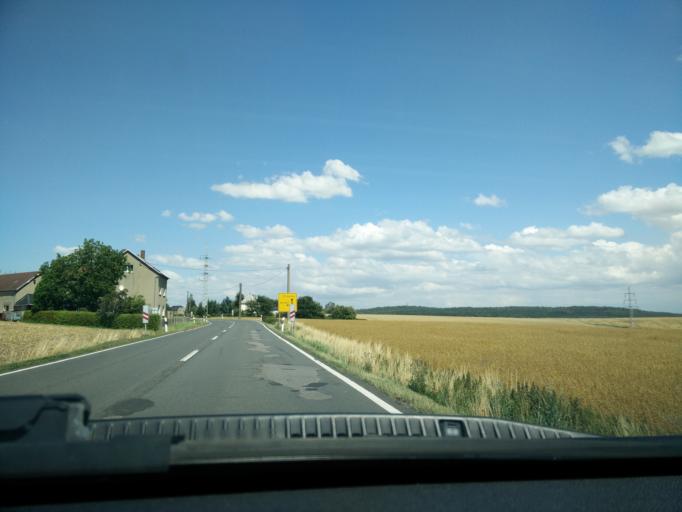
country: DE
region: Saxony
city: Narsdorf
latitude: 51.0137
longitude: 12.7261
